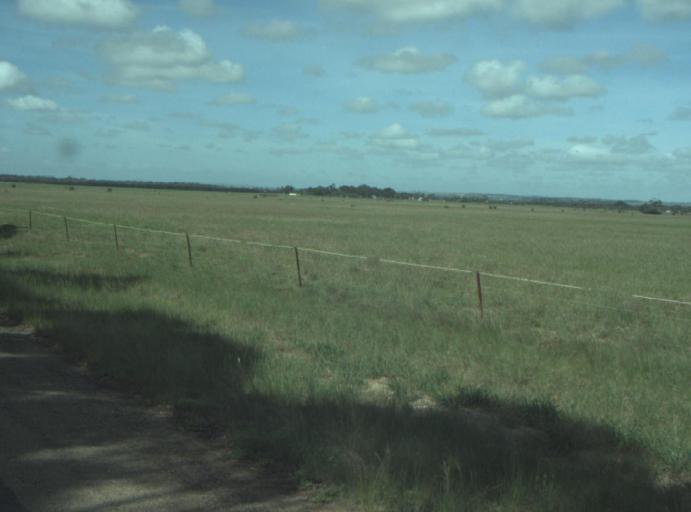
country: AU
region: Victoria
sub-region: Greater Geelong
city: Lara
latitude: -37.9752
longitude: 144.4237
